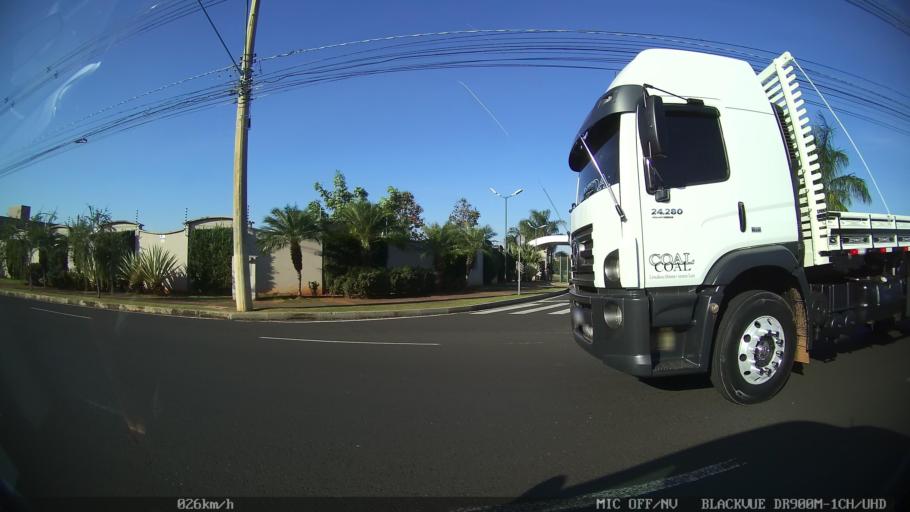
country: BR
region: Sao Paulo
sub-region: Sao Jose Do Rio Preto
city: Sao Jose do Rio Preto
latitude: -20.8604
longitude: -49.4116
